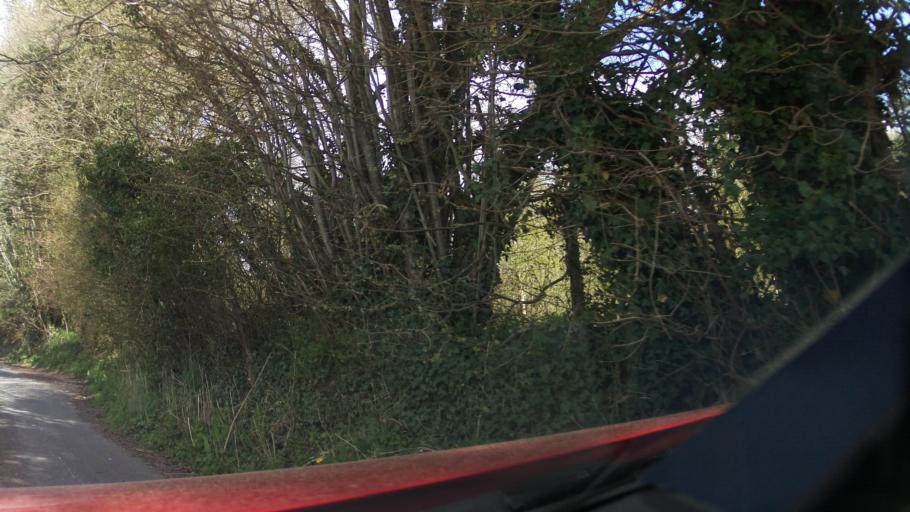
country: GB
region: England
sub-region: West Berkshire
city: Kintbury
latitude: 51.3738
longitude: -1.4876
